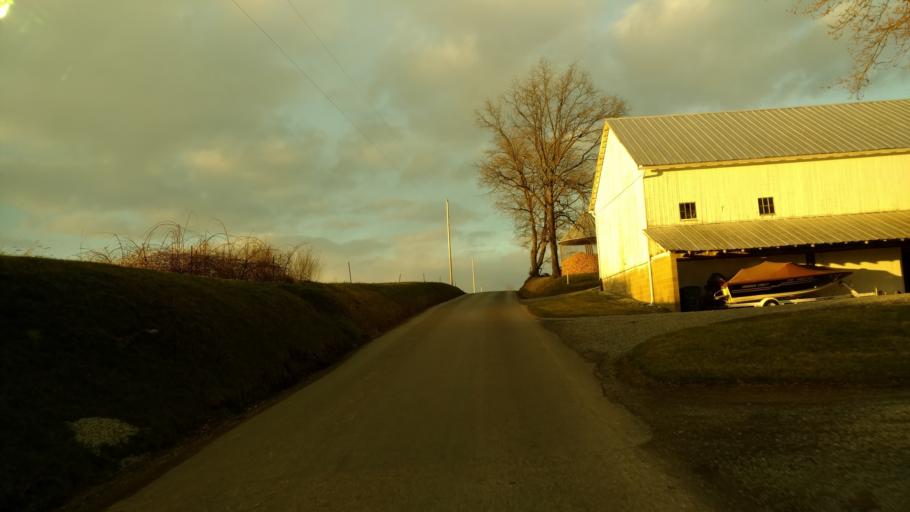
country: US
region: Ohio
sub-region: Tuscarawas County
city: Sugarcreek
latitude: 40.5199
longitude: -81.7805
